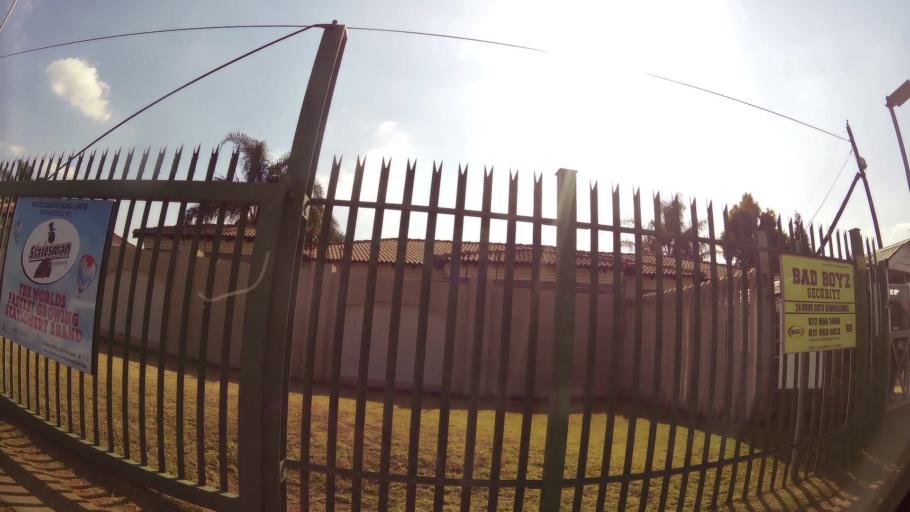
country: ZA
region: Gauteng
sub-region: Ekurhuleni Metropolitan Municipality
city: Boksburg
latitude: -26.1976
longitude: 28.2847
